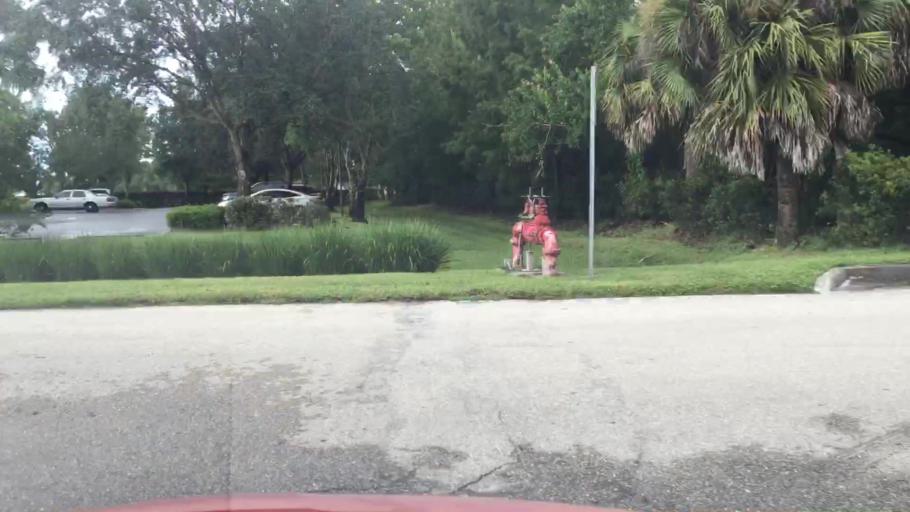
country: US
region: Florida
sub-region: Lee County
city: Gateway
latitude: 26.5481
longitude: -81.8054
